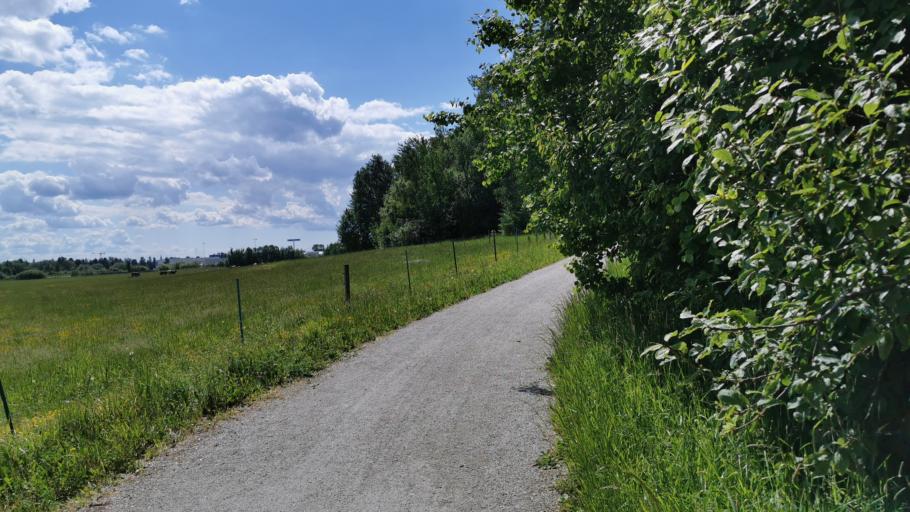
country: SE
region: OErebro
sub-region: Orebro Kommun
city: Orebro
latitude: 59.3038
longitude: 15.2111
